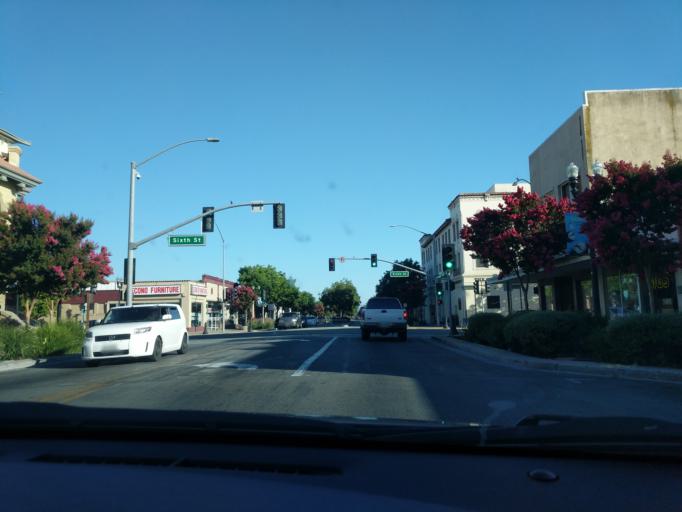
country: US
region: California
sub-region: Santa Clara County
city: Gilroy
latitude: 37.0071
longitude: -121.5688
